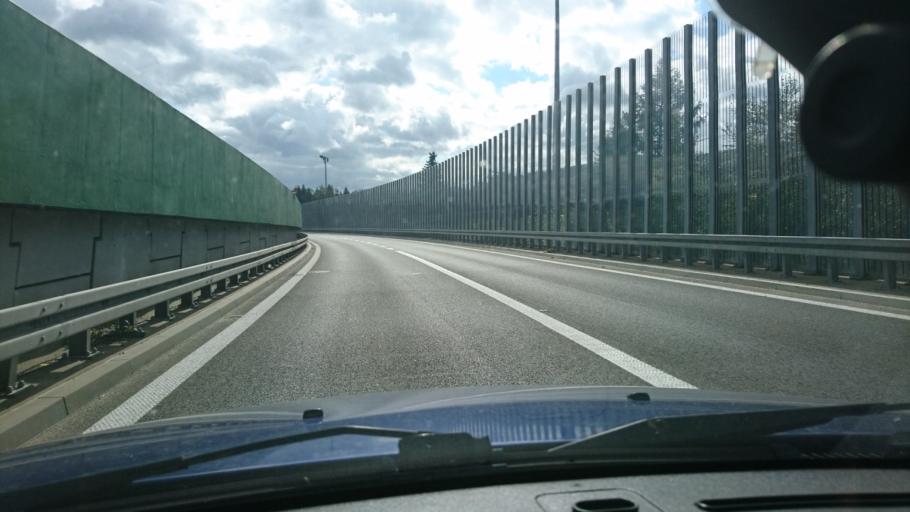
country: PL
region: Silesian Voivodeship
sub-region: Powiat bielski
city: Bystra
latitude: 49.7847
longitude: 19.0680
